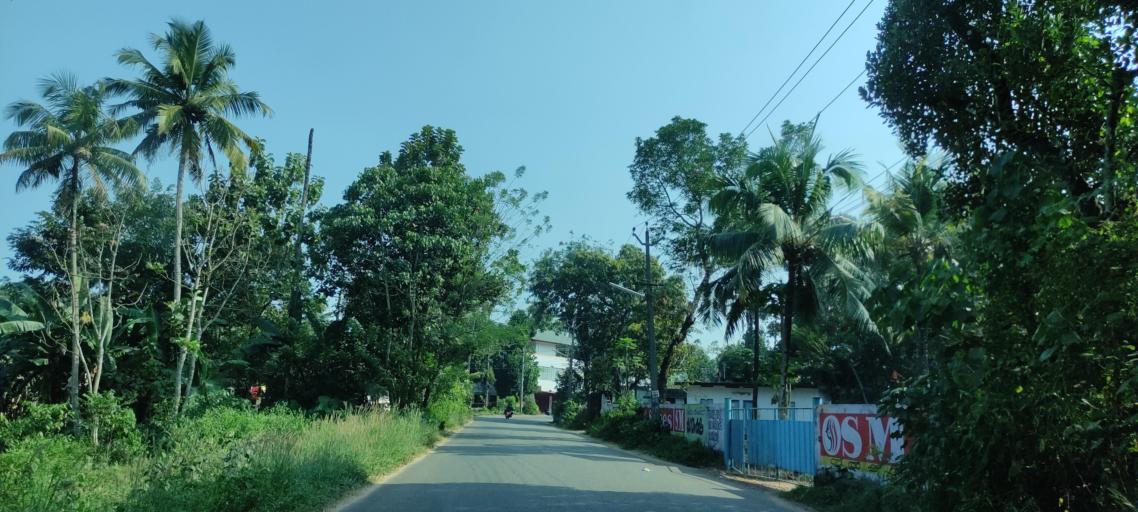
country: IN
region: Kerala
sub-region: Kollam
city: Panmana
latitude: 9.0477
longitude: 76.5750
